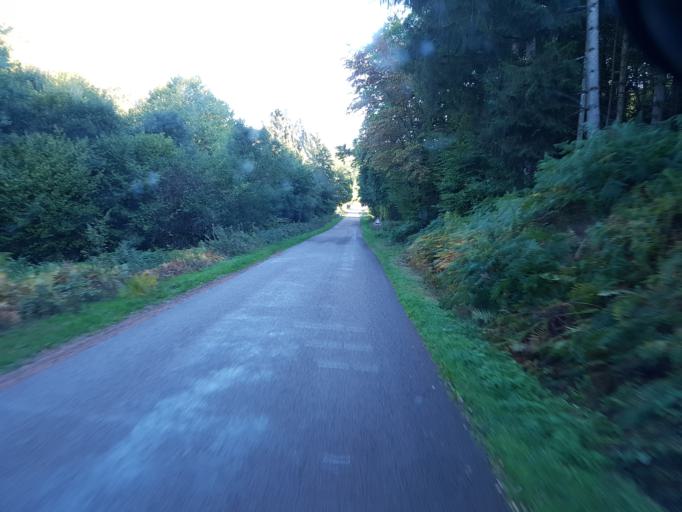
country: FR
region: Bourgogne
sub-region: Departement de la Cote-d'Or
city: Saulieu
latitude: 47.1880
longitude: 4.1777
